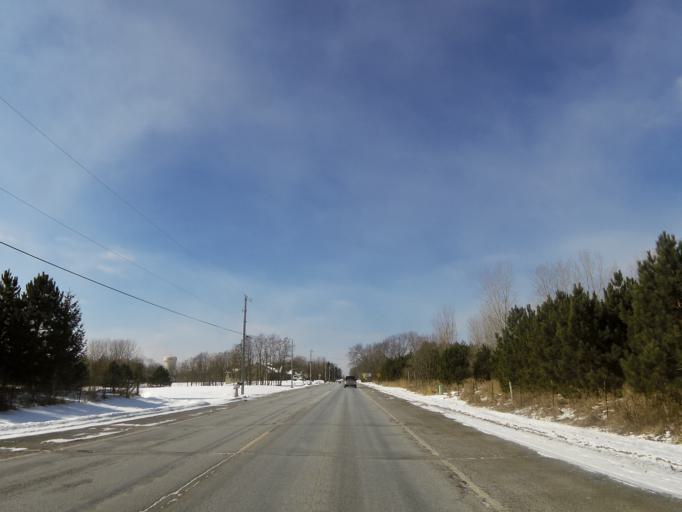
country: US
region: Minnesota
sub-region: Washington County
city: Oakdale
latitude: 44.9706
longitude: -92.9419
